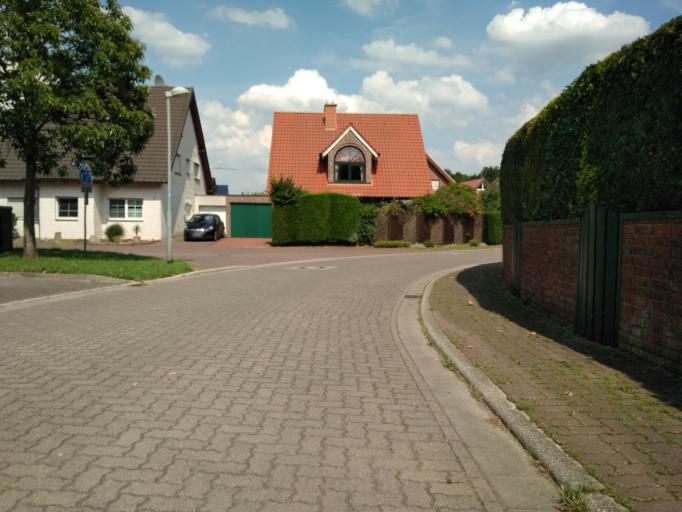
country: DE
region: North Rhine-Westphalia
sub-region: Regierungsbezirk Dusseldorf
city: Schermbeck
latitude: 51.6889
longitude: 6.8797
